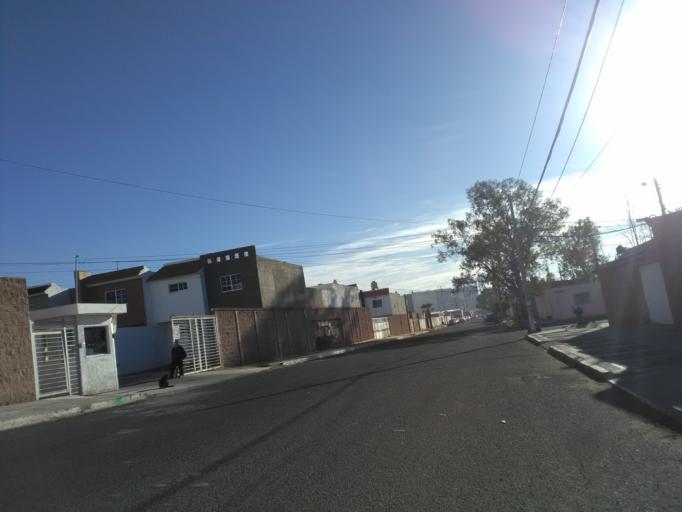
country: MX
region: Durango
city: Victoria de Durango
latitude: 24.0435
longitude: -104.6621
